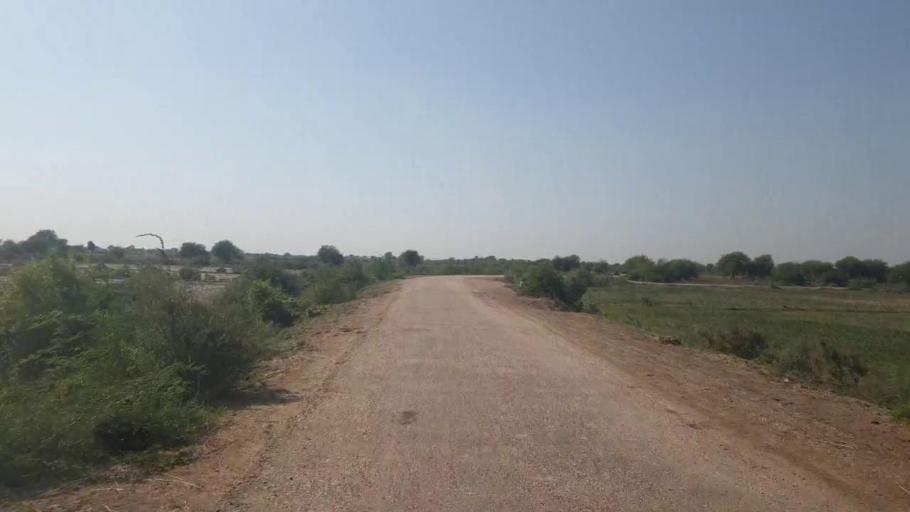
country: PK
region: Sindh
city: Badin
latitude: 24.5544
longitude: 68.8244
